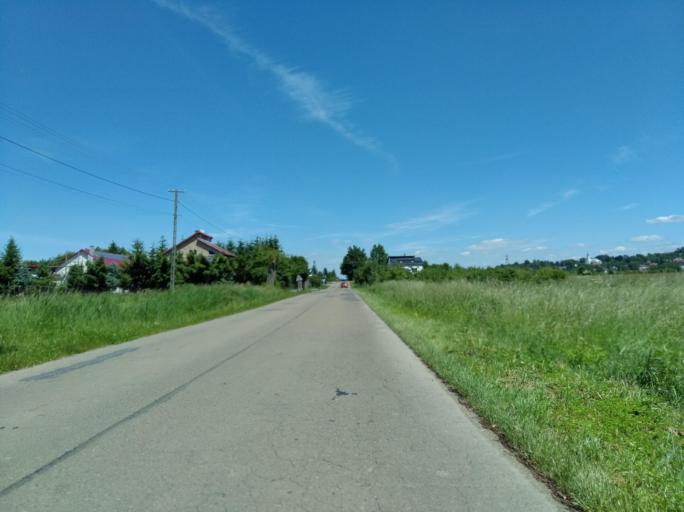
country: PL
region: Subcarpathian Voivodeship
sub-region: Powiat jasielski
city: Tarnowiec
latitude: 49.7205
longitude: 21.5608
